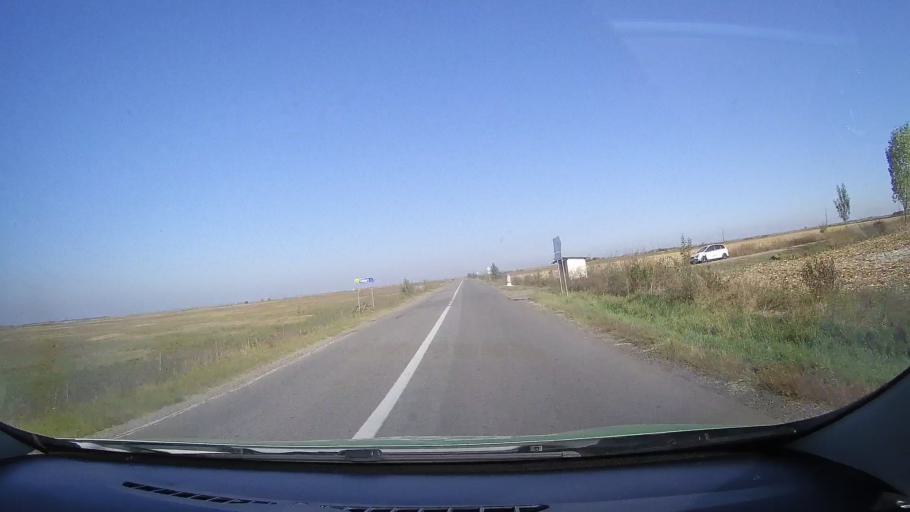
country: RO
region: Satu Mare
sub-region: Comuna Cauas
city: Cauas
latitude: 47.5358
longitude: 22.5650
